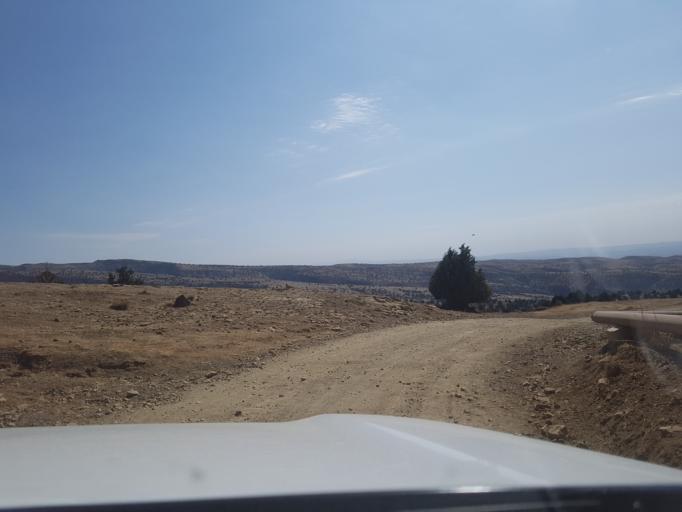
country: TM
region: Ahal
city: Baharly
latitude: 38.3201
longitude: 56.9547
